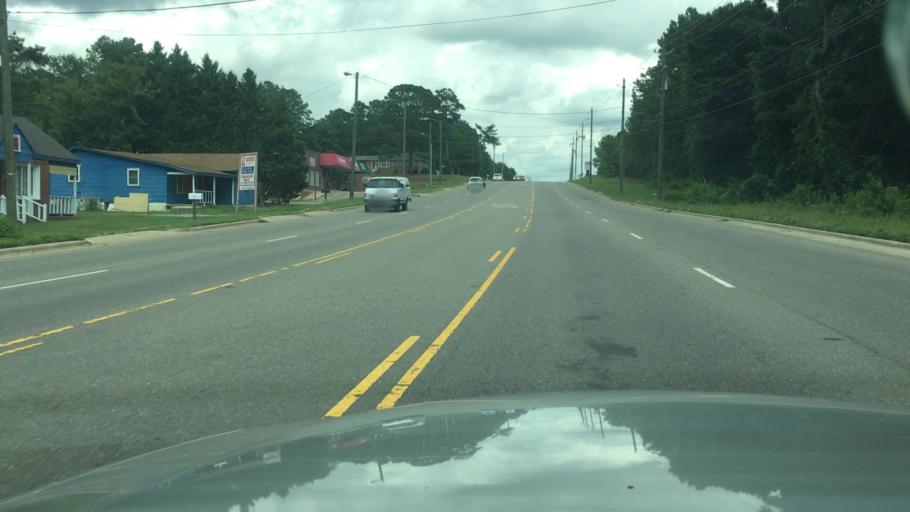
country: US
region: North Carolina
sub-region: Cumberland County
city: Hope Mills
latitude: 35.0107
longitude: -78.9494
